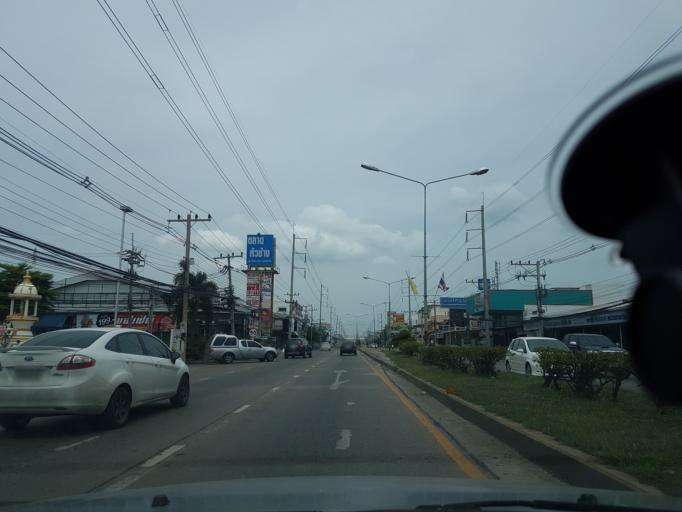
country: TH
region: Lop Buri
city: Lop Buri
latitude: 14.7921
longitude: 100.6716
